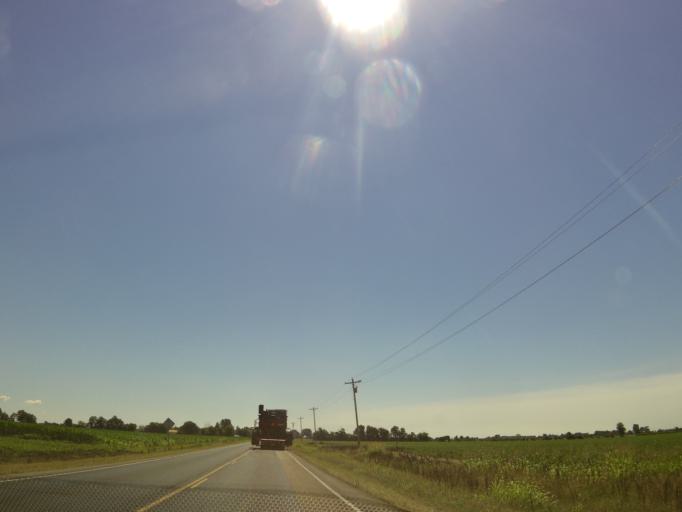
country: US
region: Missouri
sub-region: New Madrid County
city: Gideon
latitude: 36.5537
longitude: -89.8054
